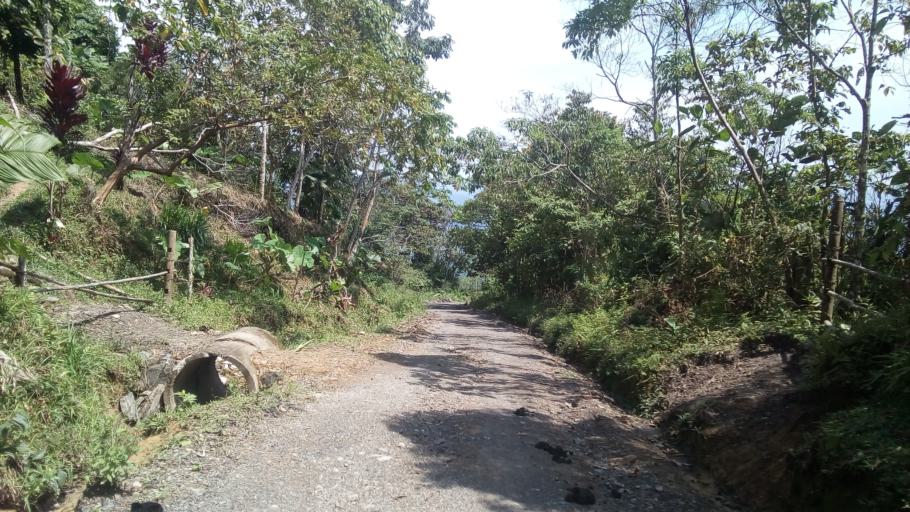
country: CO
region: Boyaca
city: Otanche
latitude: 5.6258
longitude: -74.2347
